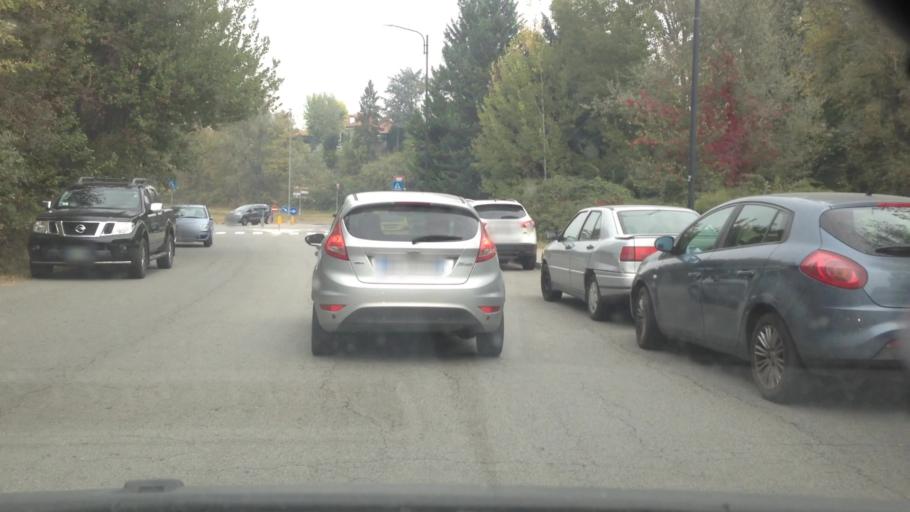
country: IT
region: Piedmont
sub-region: Provincia di Asti
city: Asti
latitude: 44.9149
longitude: 8.1974
